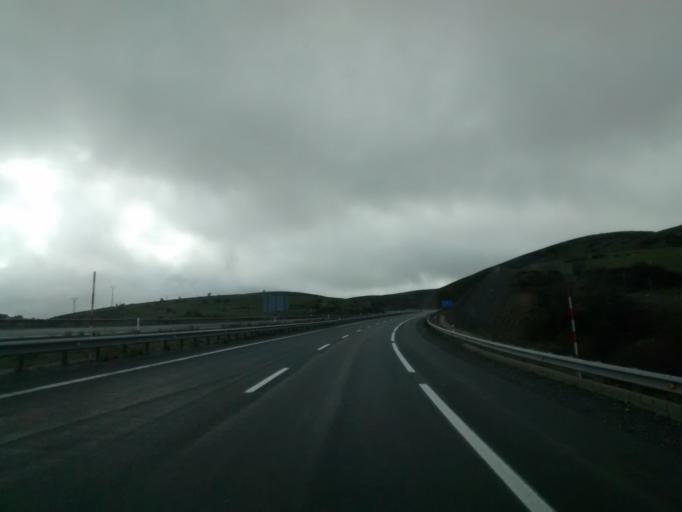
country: ES
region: Cantabria
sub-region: Provincia de Cantabria
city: Villaescusa
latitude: 42.9309
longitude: -4.1226
